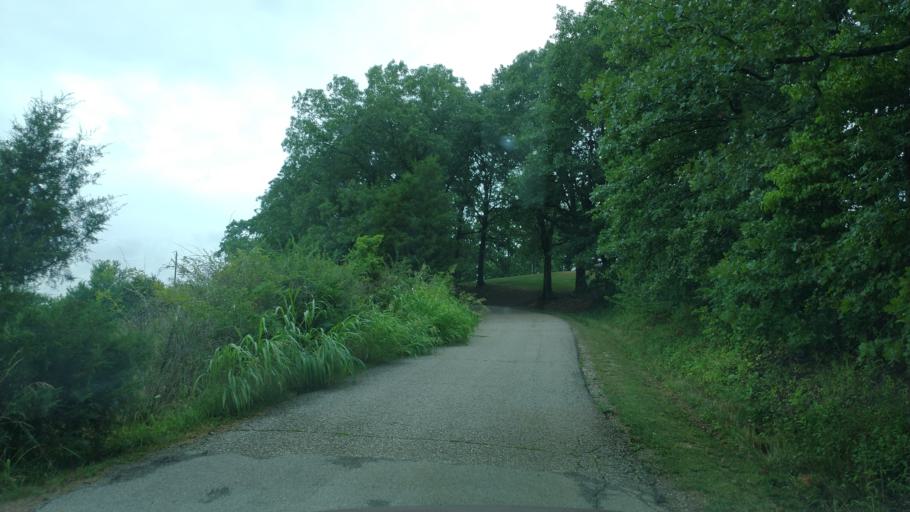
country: US
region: West Virginia
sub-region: Mason County
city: New Haven
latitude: 38.9244
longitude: -81.9552
